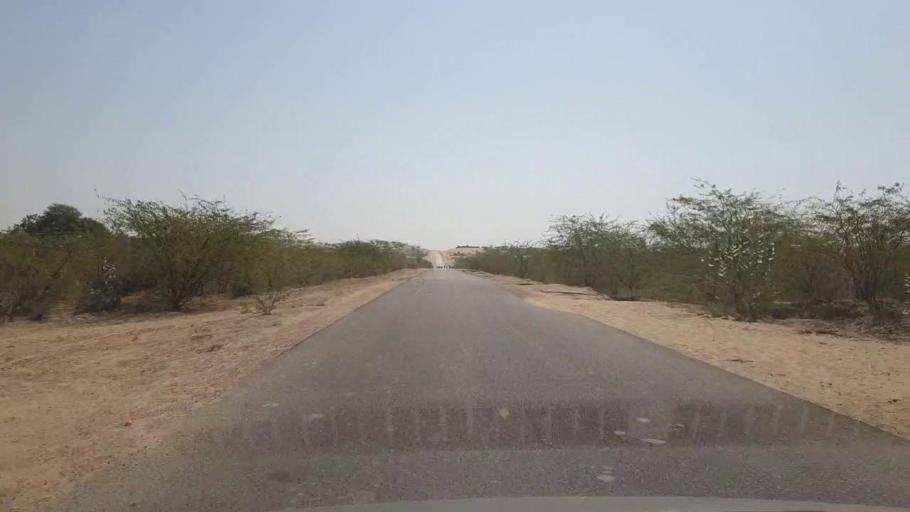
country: PK
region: Sindh
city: Chor
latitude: 25.5798
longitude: 70.1894
